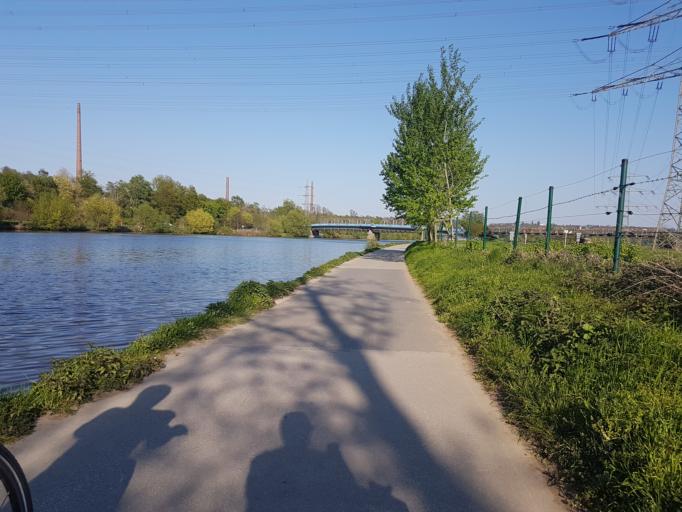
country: DE
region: North Rhine-Westphalia
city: Hattingen
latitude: 51.4307
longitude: 7.1209
